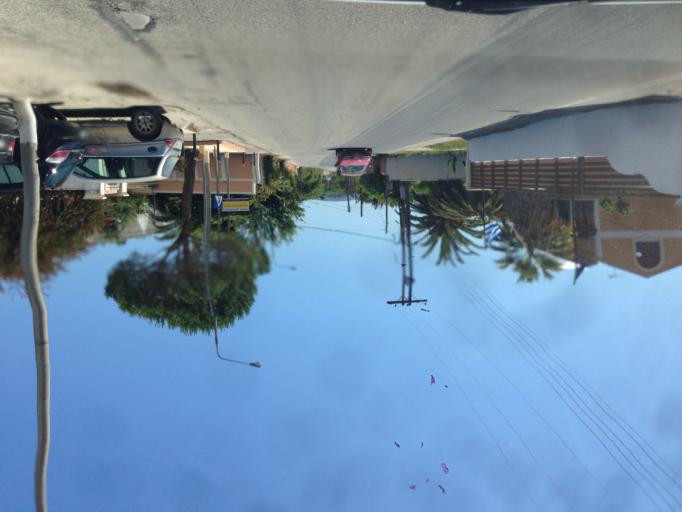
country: GR
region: Ionian Islands
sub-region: Nomos Kerkyras
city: Agios Georgis
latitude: 39.7817
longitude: 19.7086
